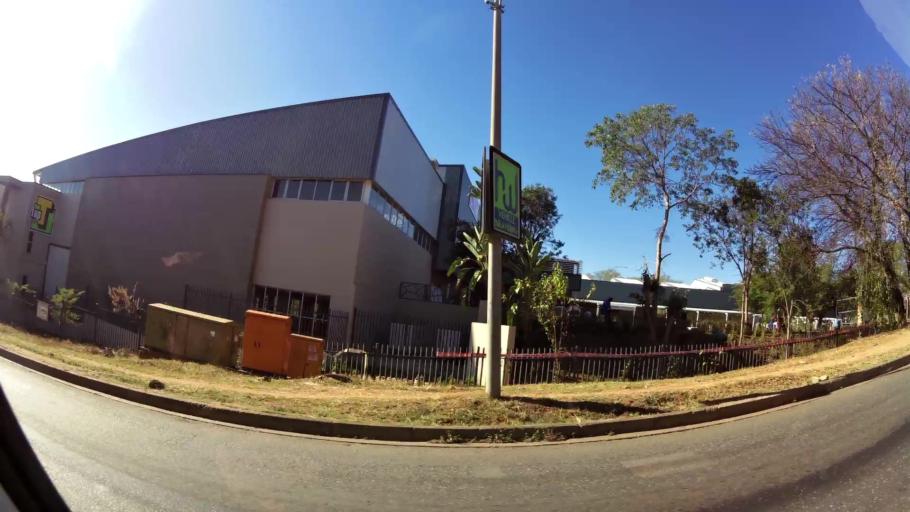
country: ZA
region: Limpopo
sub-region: Mopani District Municipality
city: Tzaneen
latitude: -23.8313
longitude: 30.1651
